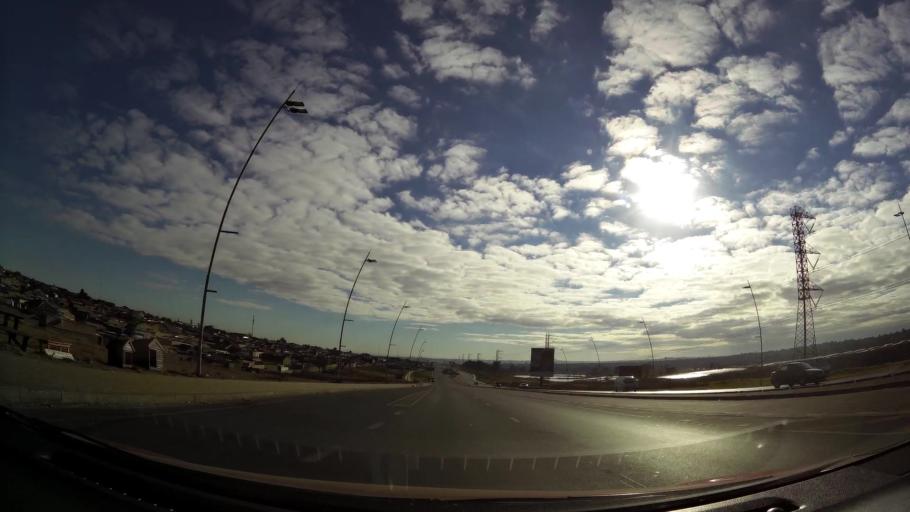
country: ZA
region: Gauteng
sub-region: City of Johannesburg Metropolitan Municipality
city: Modderfontein
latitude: -26.0554
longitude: 28.1834
